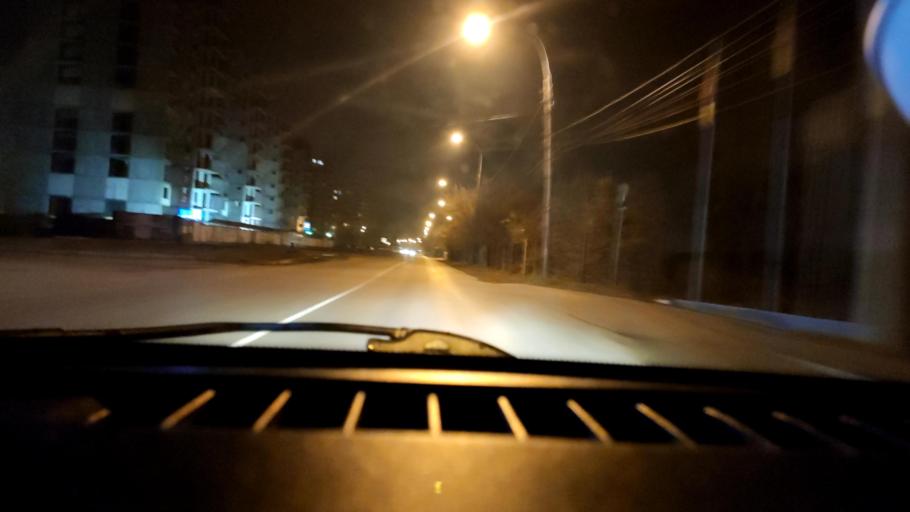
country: RU
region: Samara
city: Rozhdestveno
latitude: 53.1490
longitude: 50.0644
